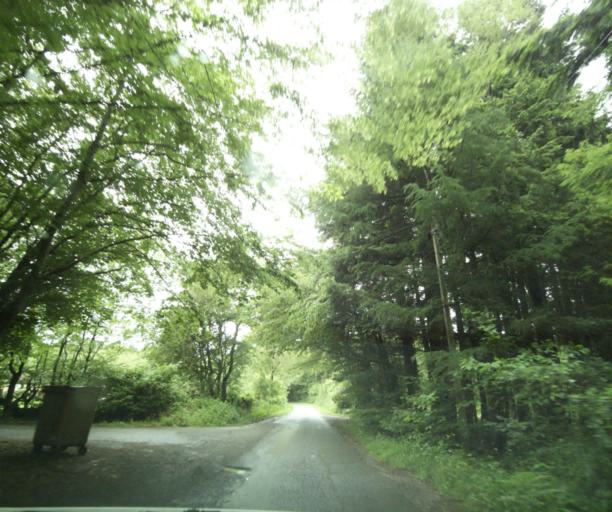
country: FR
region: Bourgogne
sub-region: Departement de Saone-et-Loire
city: Ciry-le-Noble
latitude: 46.5223
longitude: 4.3027
